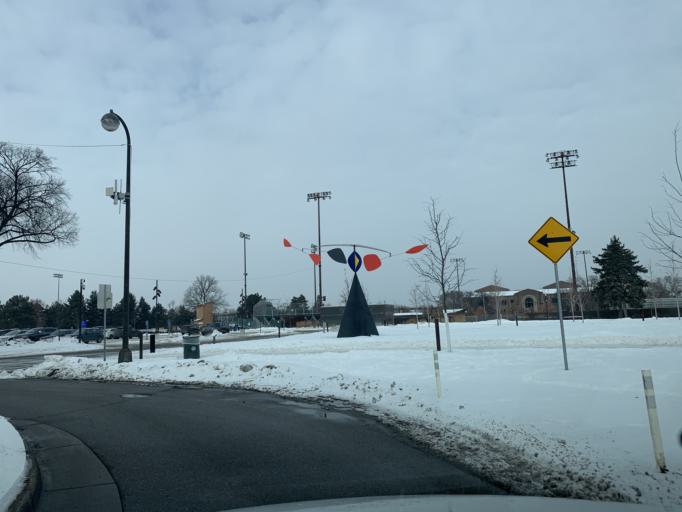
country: US
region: Minnesota
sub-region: Hennepin County
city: Minneapolis
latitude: 44.9698
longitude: -93.2904
